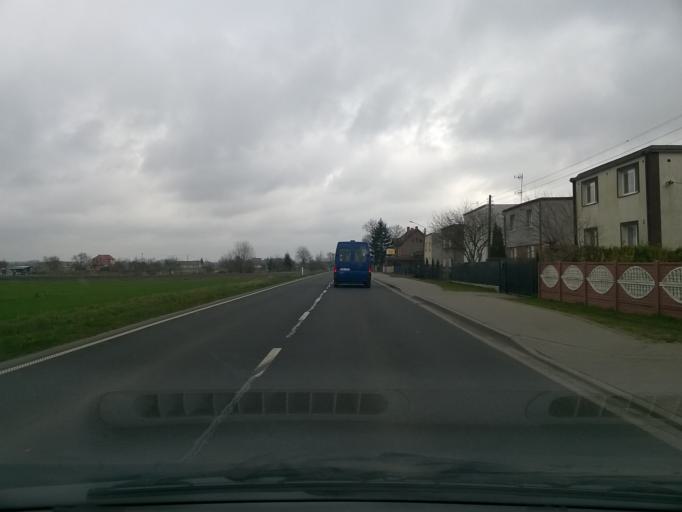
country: PL
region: Kujawsko-Pomorskie
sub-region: Powiat nakielski
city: Kcynia
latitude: 52.9892
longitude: 17.6023
